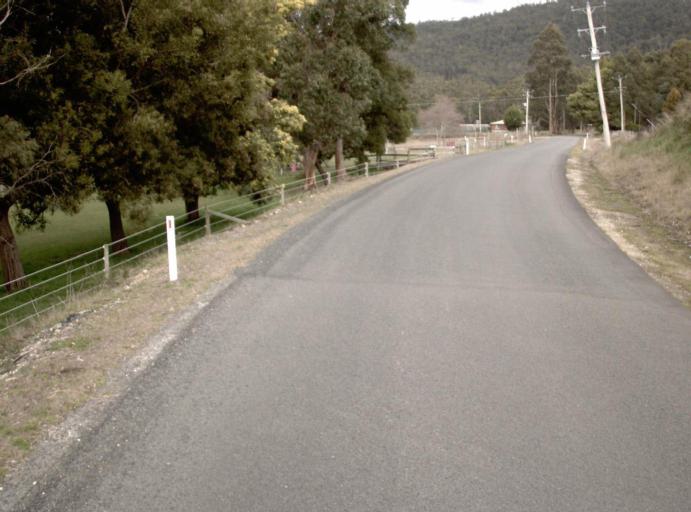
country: AU
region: Tasmania
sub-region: Launceston
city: Mayfield
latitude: -41.2630
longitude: 147.1605
